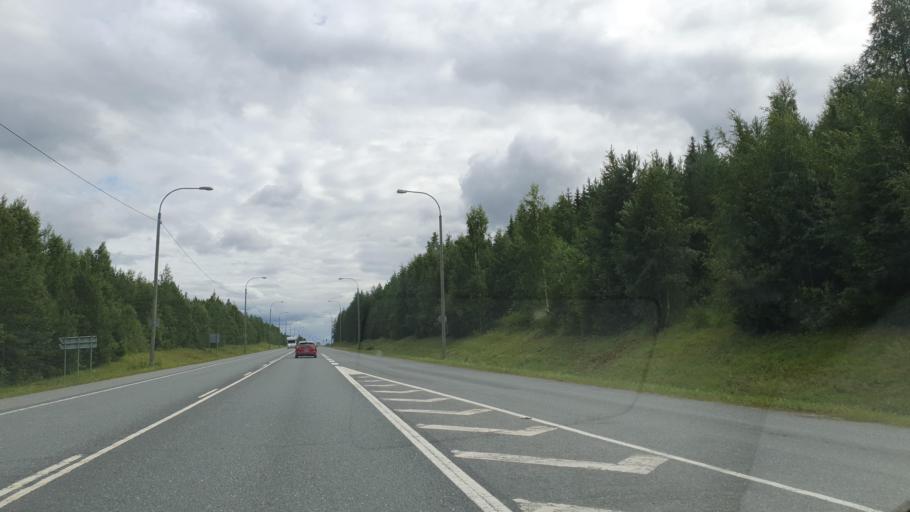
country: FI
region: Northern Savo
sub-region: Ylae-Savo
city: Iisalmi
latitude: 63.5879
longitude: 27.2273
